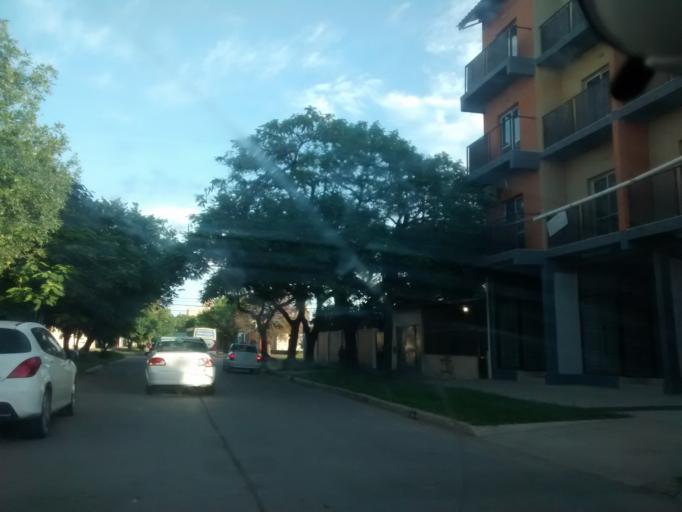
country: AR
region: Chaco
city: Resistencia
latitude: -27.4657
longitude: -58.9771
